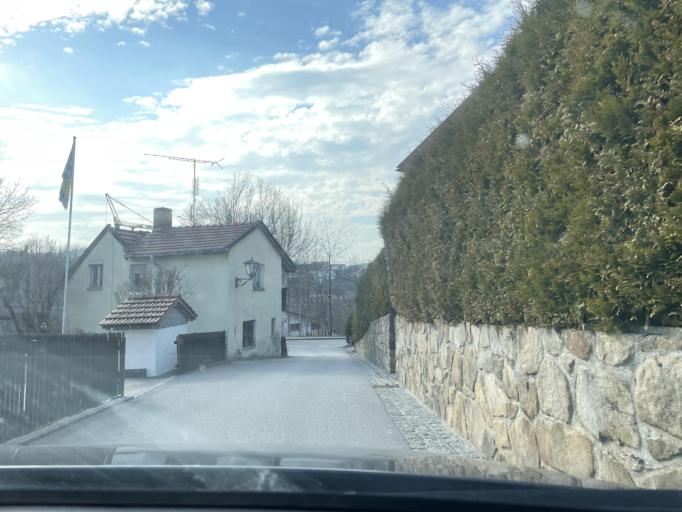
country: DE
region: Bavaria
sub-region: Lower Bavaria
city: Viechtach
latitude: 49.0807
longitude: 12.8935
